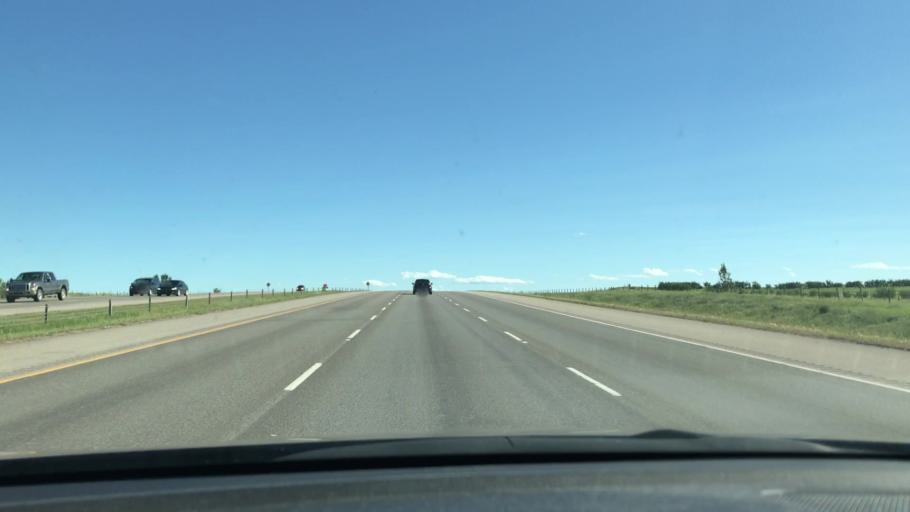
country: CA
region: Alberta
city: Crossfield
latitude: 51.5137
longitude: -114.0253
